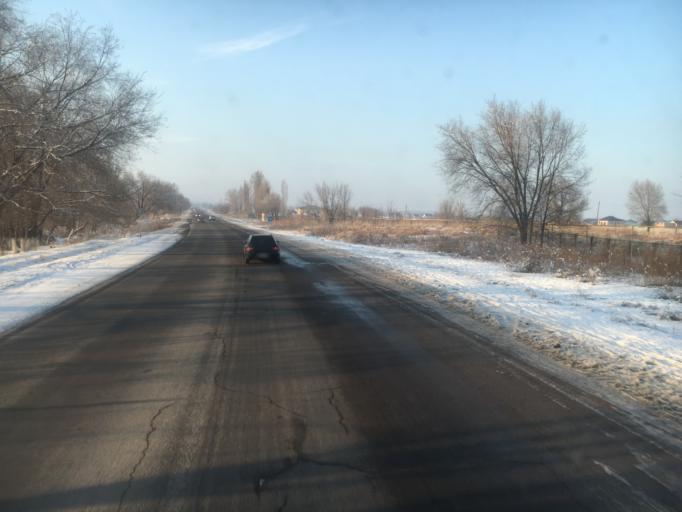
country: KZ
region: Almaty Oblysy
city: Burunday
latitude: 43.3412
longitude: 76.6583
